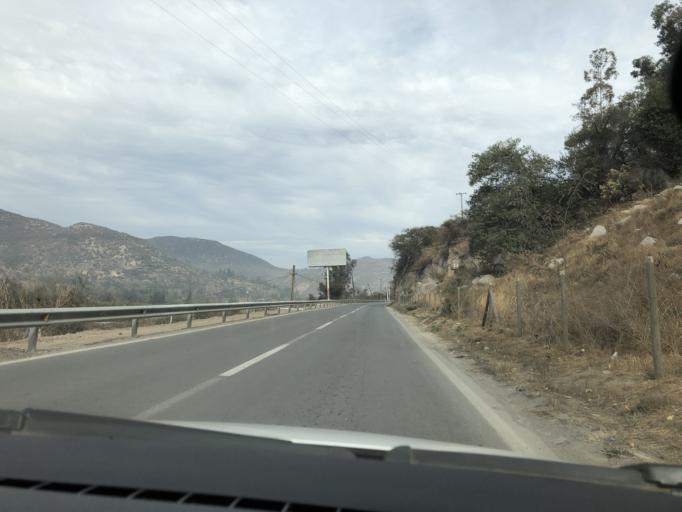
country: CL
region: Santiago Metropolitan
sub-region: Provincia de Cordillera
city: Puente Alto
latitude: -33.5943
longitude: -70.4902
